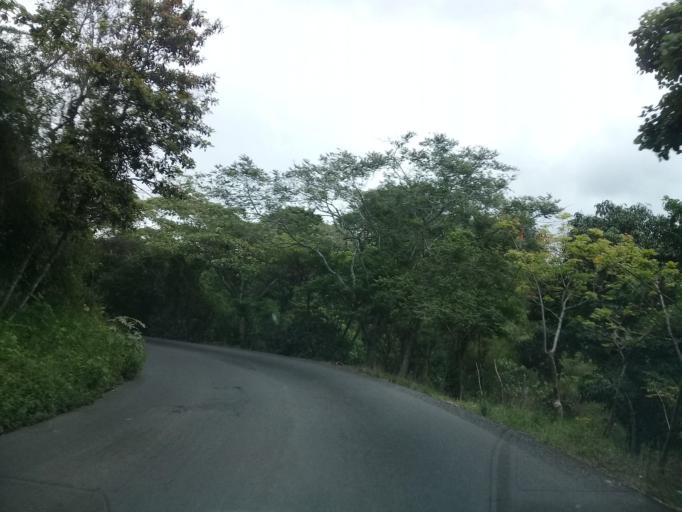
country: MX
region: Veracruz
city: El Castillo
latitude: 19.5620
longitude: -96.8489
